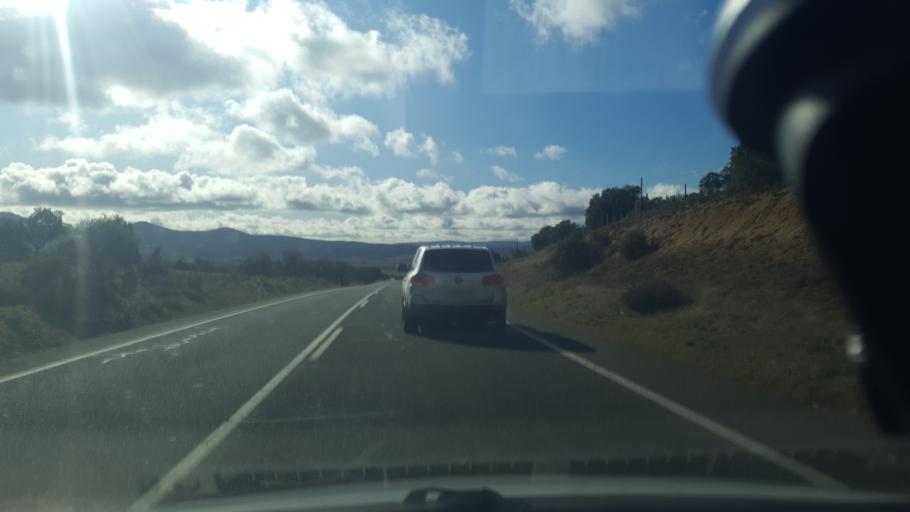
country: ES
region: Castille and Leon
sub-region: Provincia de Segovia
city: Valdeprados
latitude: 40.8420
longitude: -4.2636
